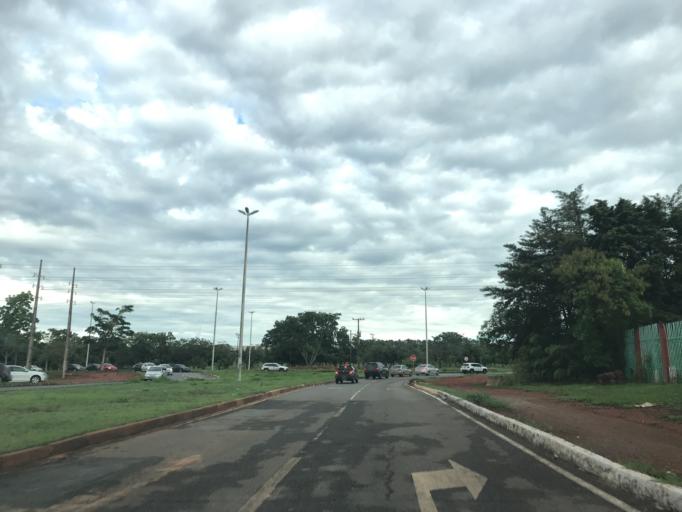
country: BR
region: Federal District
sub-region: Brasilia
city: Brasilia
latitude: -15.8144
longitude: -47.9218
